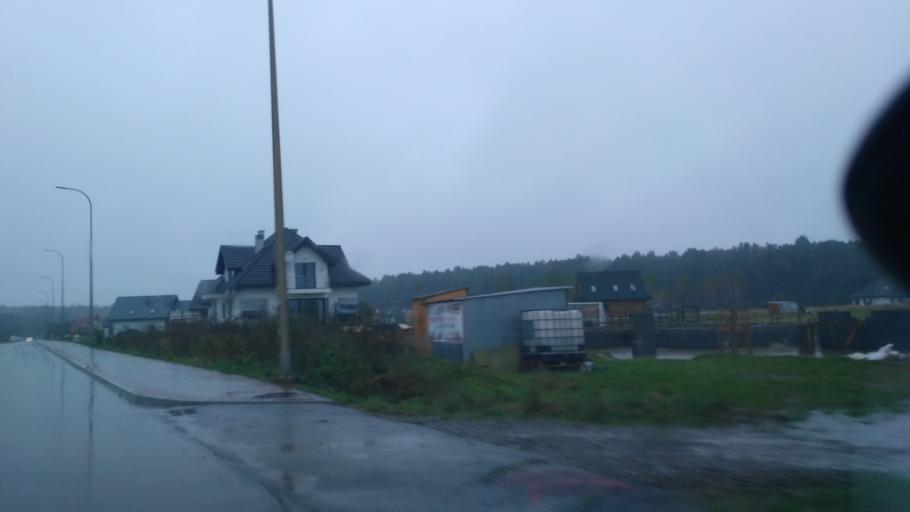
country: PL
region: Subcarpathian Voivodeship
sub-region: Powiat krosnienski
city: Kroscienko Wyzne
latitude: 49.6669
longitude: 21.8039
